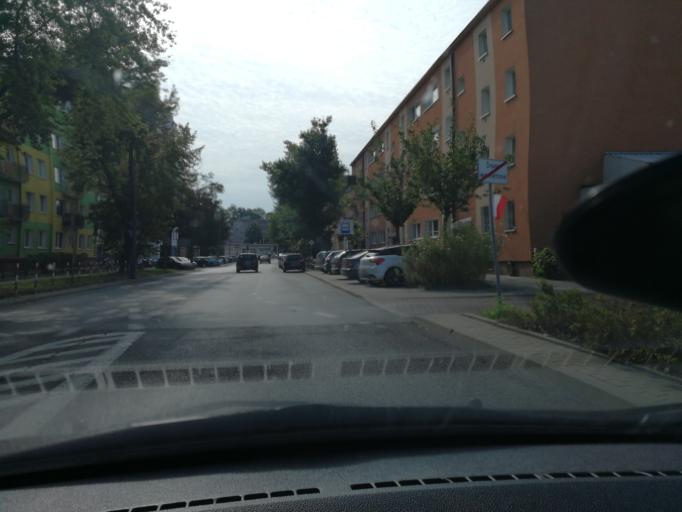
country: PL
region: Masovian Voivodeship
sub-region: Warszawa
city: Bemowo
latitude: 52.2357
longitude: 20.9393
